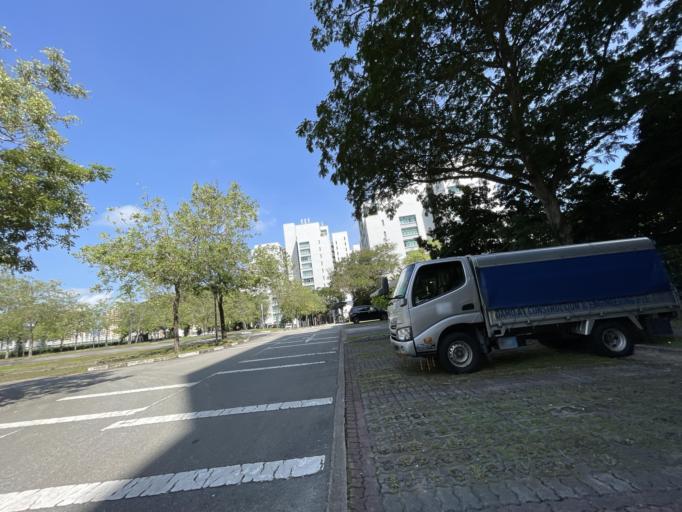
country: SG
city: Singapore
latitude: 1.3013
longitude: 103.7679
